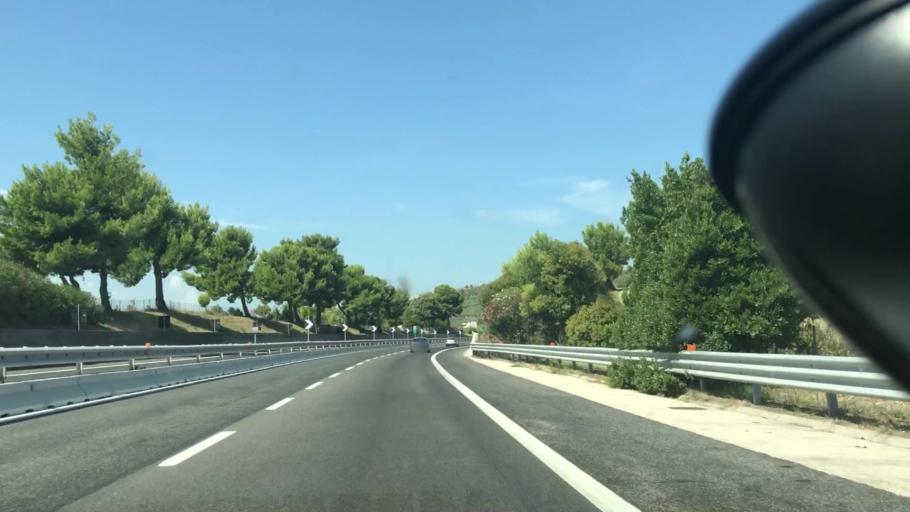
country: IT
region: Abruzzo
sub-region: Provincia di Chieti
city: Marina di Vasto
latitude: 42.0804
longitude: 14.7037
